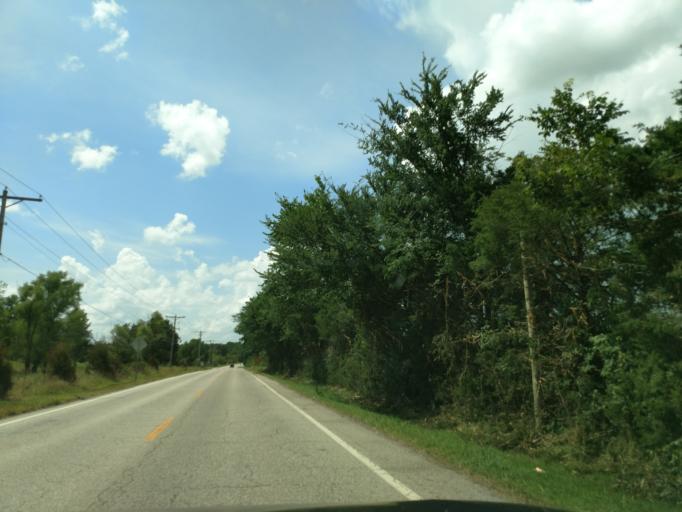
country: US
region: Arkansas
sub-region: Boone County
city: Harrison
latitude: 36.2577
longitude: -93.2267
